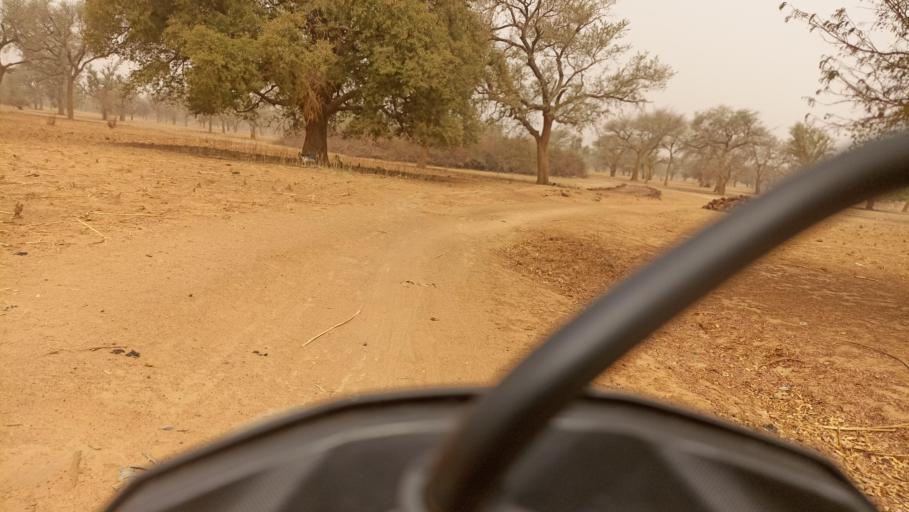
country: BF
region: Nord
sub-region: Province du Zondoma
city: Gourcy
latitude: 13.2487
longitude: -2.5963
